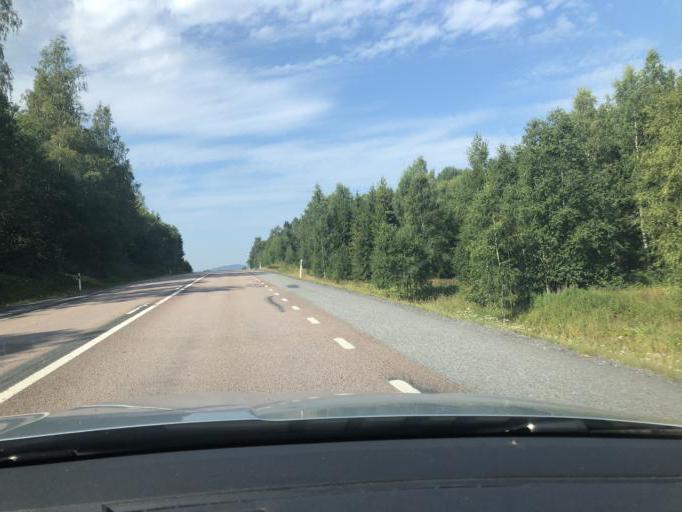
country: SE
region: Vaesternorrland
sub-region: Haernoesands Kommun
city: Haernoesand
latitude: 62.7941
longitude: 17.8954
